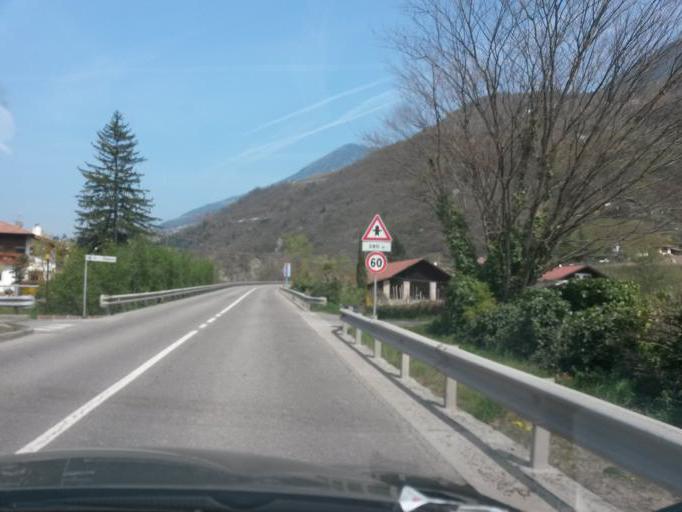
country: IT
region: Trentino-Alto Adige
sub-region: Bolzano
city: Sinigo
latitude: 46.6522
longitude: 11.1818
